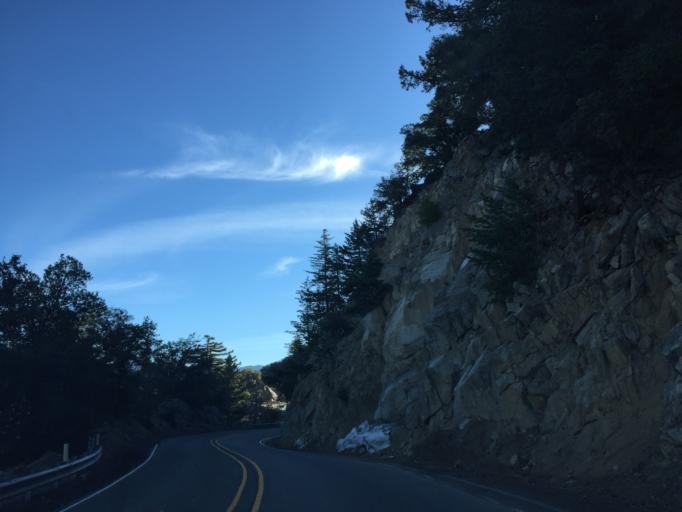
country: US
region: California
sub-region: San Bernardino County
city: Big Bear Lake
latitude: 34.1575
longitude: -116.9527
